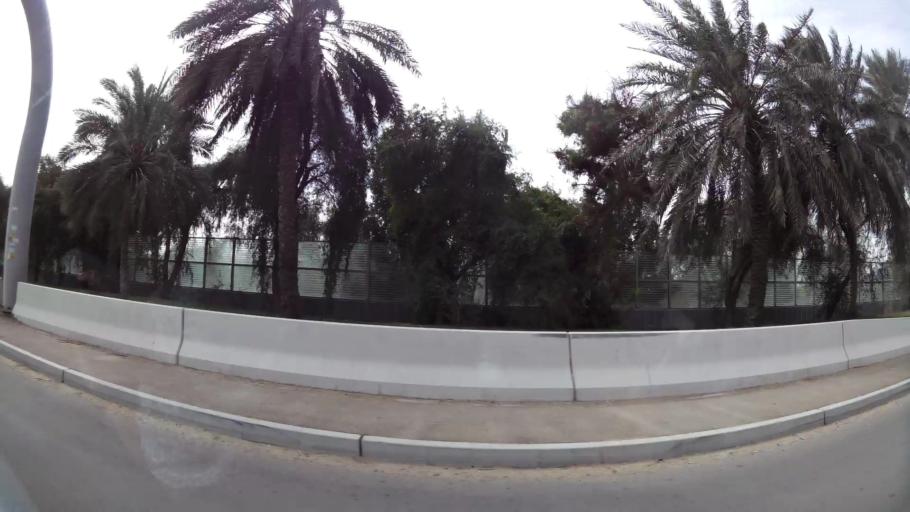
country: AE
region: Abu Dhabi
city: Abu Dhabi
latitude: 24.3958
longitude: 54.5129
